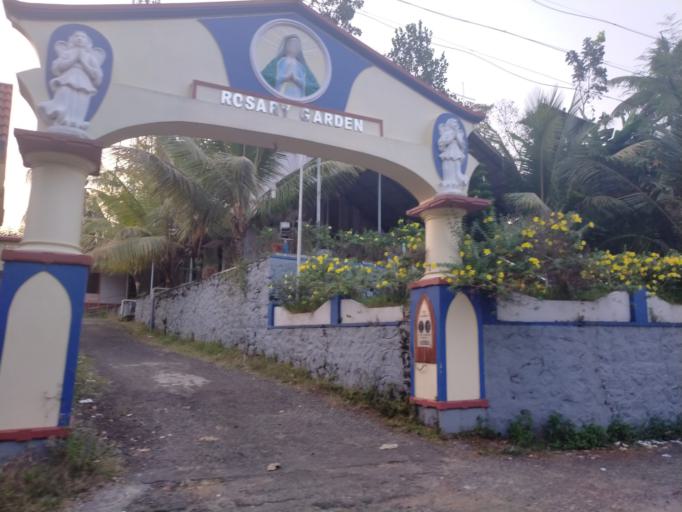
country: IN
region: Kerala
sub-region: Kottayam
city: Palackattumala
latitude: 9.7030
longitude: 76.5476
